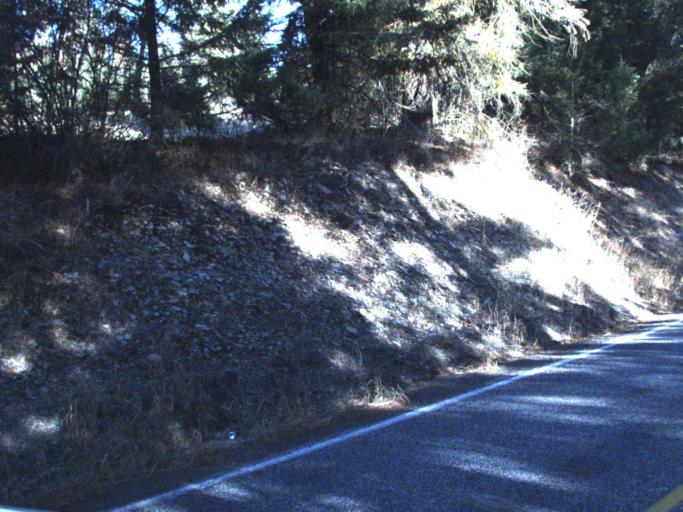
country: US
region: Washington
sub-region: Ferry County
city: Republic
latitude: 48.6171
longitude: -118.7314
